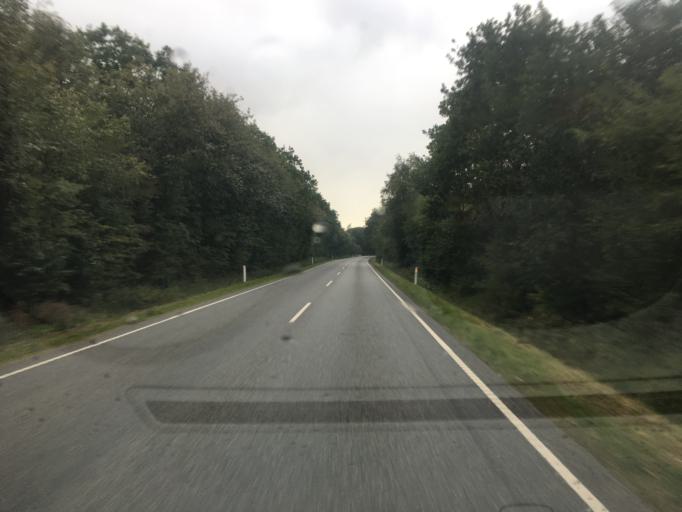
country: DK
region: South Denmark
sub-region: Tonder Kommune
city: Logumkloster
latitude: 55.0592
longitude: 8.9063
